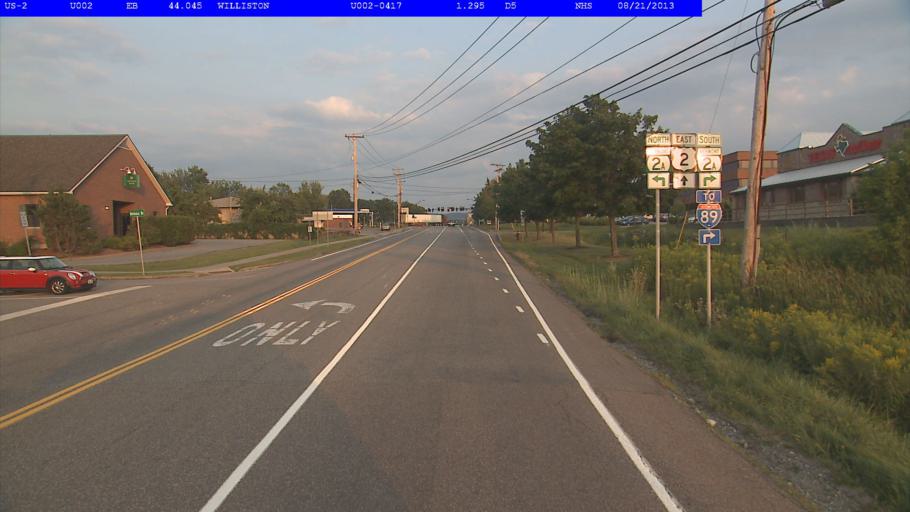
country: US
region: Vermont
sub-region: Chittenden County
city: Essex Junction
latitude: 44.4505
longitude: -73.1132
